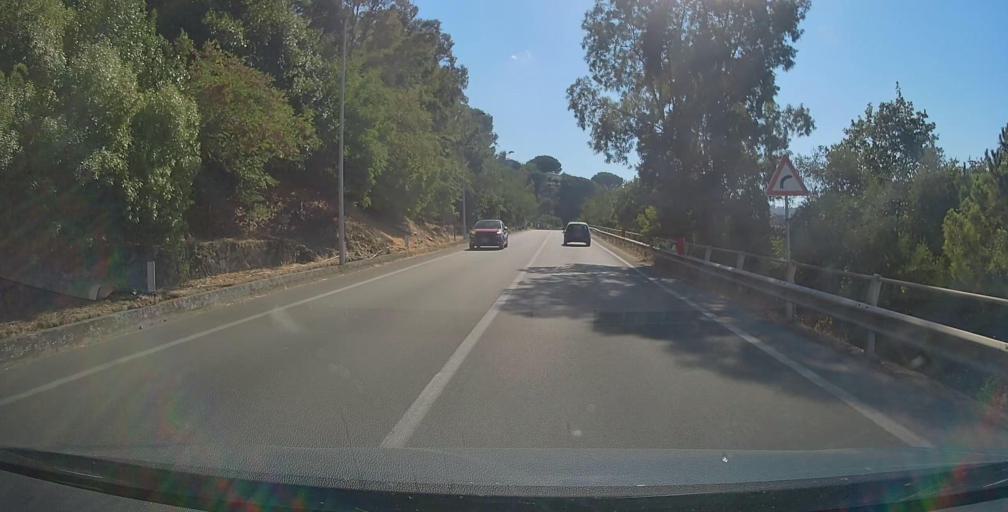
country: IT
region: Sicily
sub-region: Messina
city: Naso
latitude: 38.1527
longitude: 14.7740
